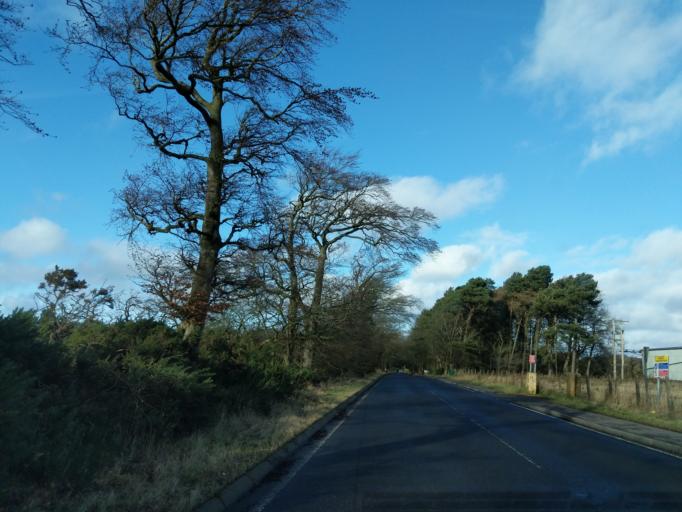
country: GB
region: Scotland
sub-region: West Lothian
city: Kirknewton
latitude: 55.8770
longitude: -3.4124
